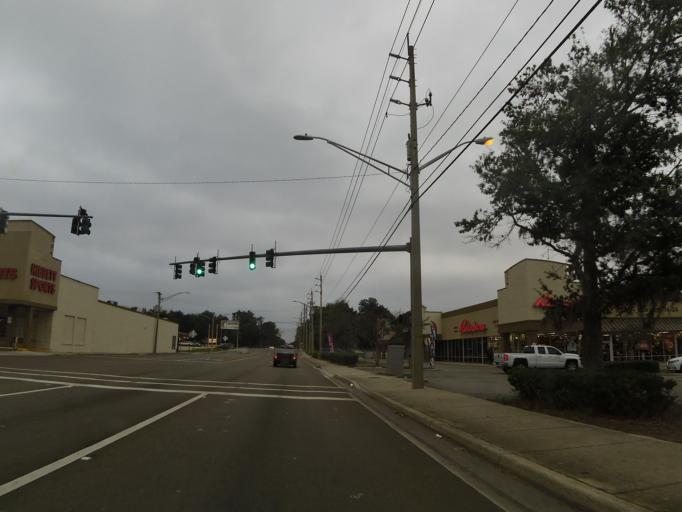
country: US
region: Florida
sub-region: Clay County
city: Bellair-Meadowbrook Terrace
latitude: 30.2705
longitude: -81.7374
